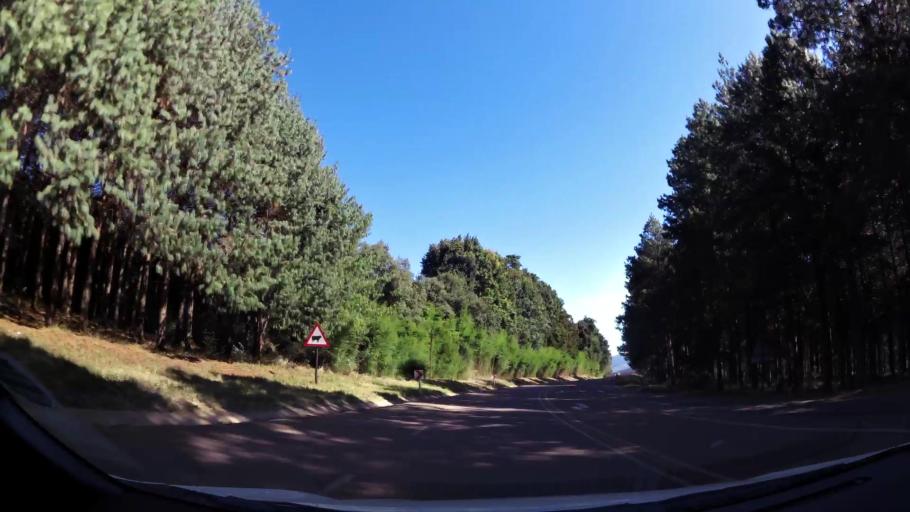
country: ZA
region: Limpopo
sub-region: Capricorn District Municipality
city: Mankoeng
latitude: -23.9271
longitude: 29.9606
